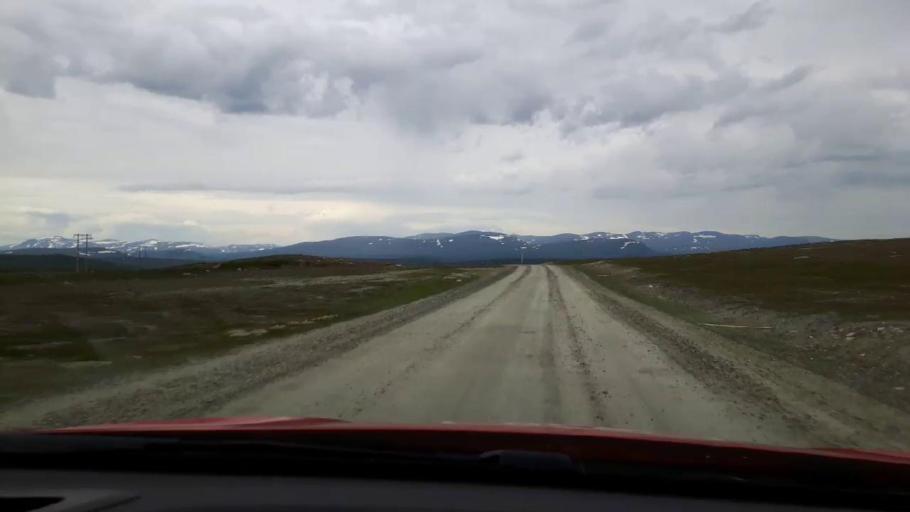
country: SE
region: Jaemtland
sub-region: Are Kommun
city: Are
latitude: 62.7642
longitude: 12.7658
